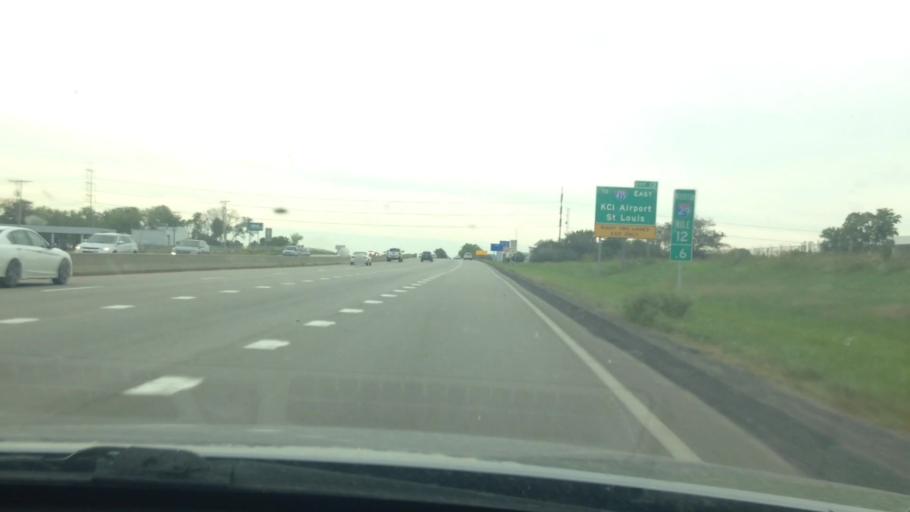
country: US
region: Missouri
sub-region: Platte County
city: Weatherby Lake
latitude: 39.3014
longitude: -94.6853
